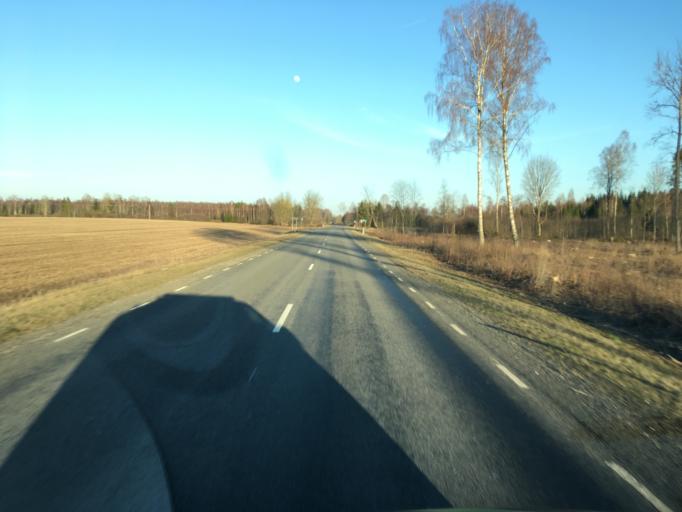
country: EE
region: Raplamaa
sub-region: Rapla vald
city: Rapla
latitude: 59.0727
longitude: 24.8952
